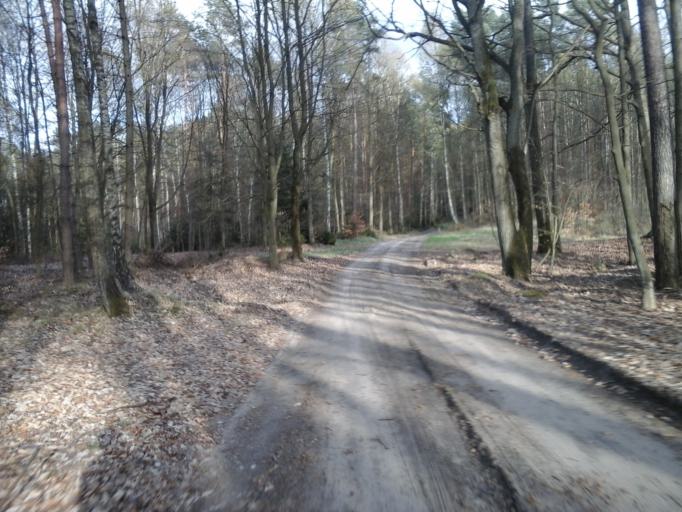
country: PL
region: West Pomeranian Voivodeship
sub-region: Powiat choszczenski
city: Bierzwnik
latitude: 53.0222
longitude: 15.5937
